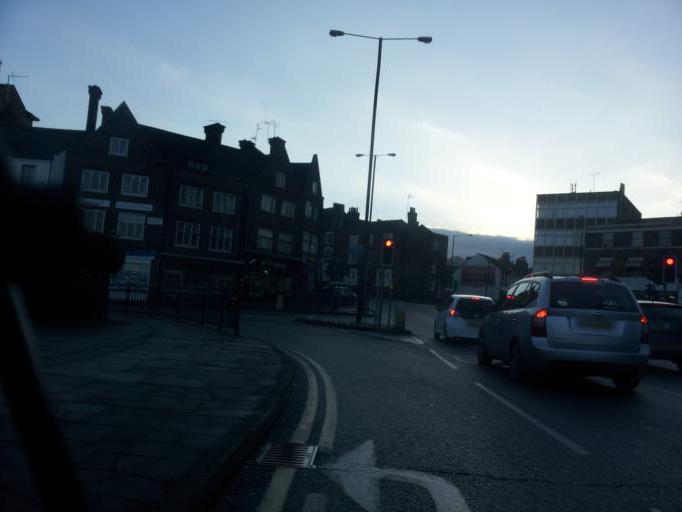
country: GB
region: England
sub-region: Medway
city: Rochester
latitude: 51.3860
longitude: 0.5082
